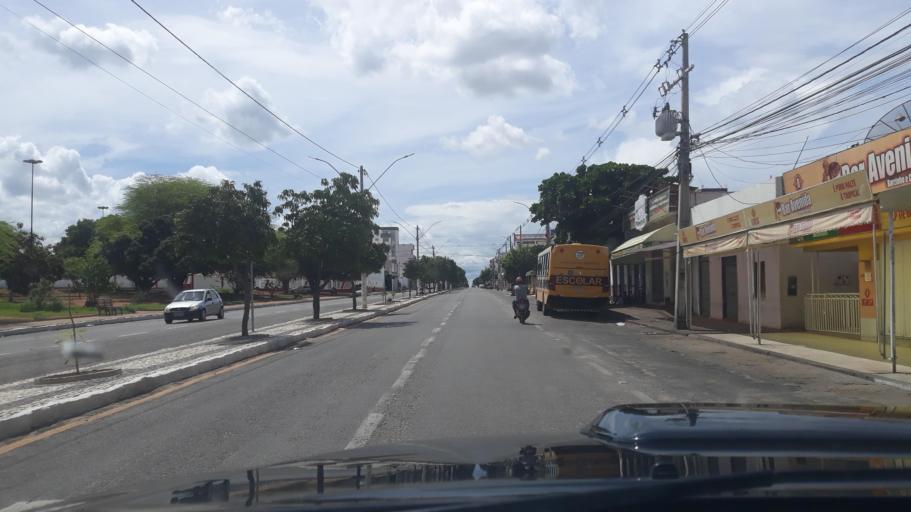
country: BR
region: Bahia
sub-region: Guanambi
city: Guanambi
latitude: -14.2189
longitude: -42.7797
